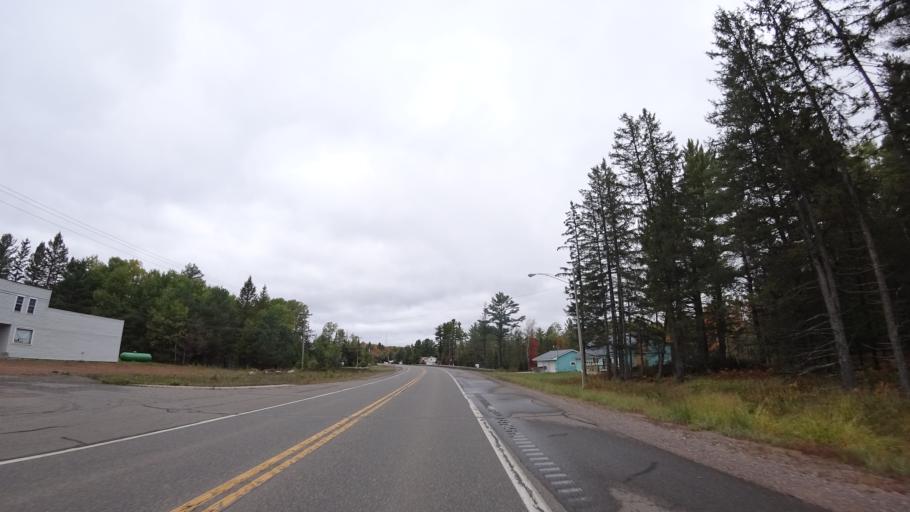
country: US
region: Michigan
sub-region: Marquette County
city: West Ishpeming
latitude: 46.4976
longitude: -87.9400
